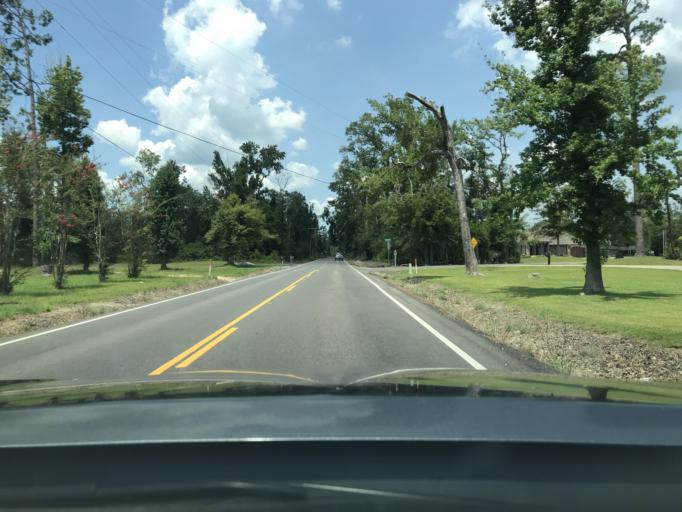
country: US
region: Louisiana
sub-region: Calcasieu Parish
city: Moss Bluff
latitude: 30.3156
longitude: -93.1837
